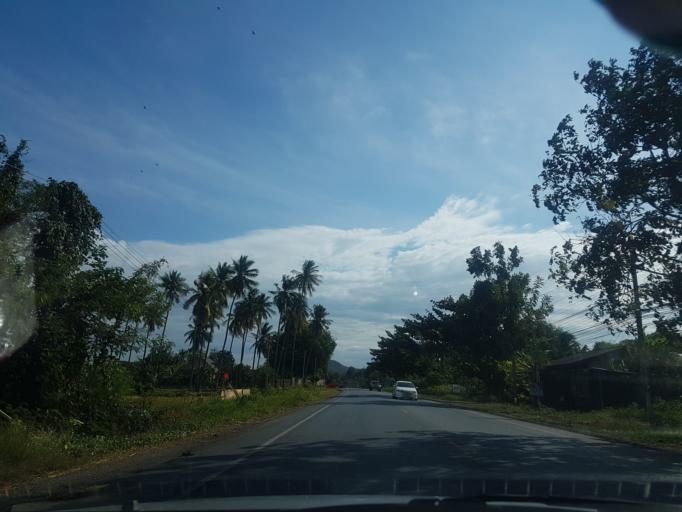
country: TH
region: Sara Buri
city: Phra Phutthabat
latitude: 14.8023
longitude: 100.7479
